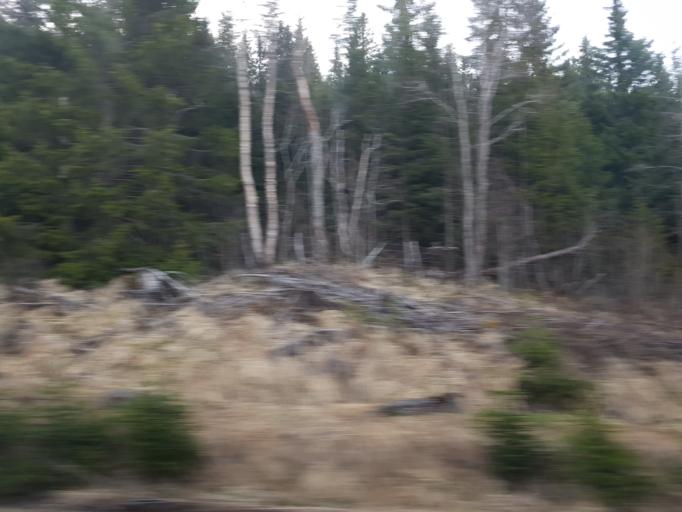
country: NO
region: Sor-Trondelag
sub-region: Rennebu
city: Berkak
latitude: 62.9126
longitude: 10.1394
